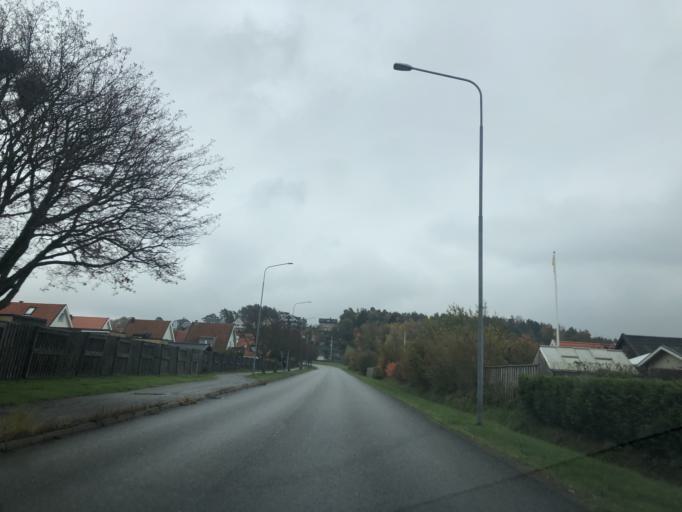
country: SE
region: Vaestra Goetaland
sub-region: Goteborg
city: Majorna
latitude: 57.6348
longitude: 11.9155
